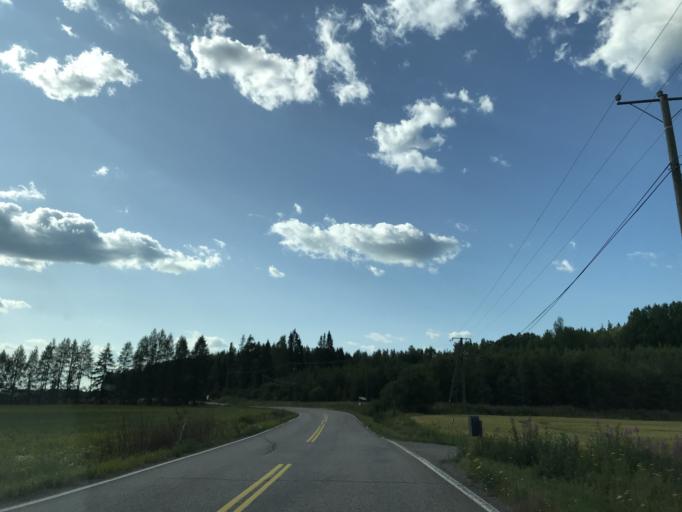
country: FI
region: Uusimaa
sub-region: Helsinki
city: Nurmijaervi
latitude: 60.4508
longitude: 24.6410
